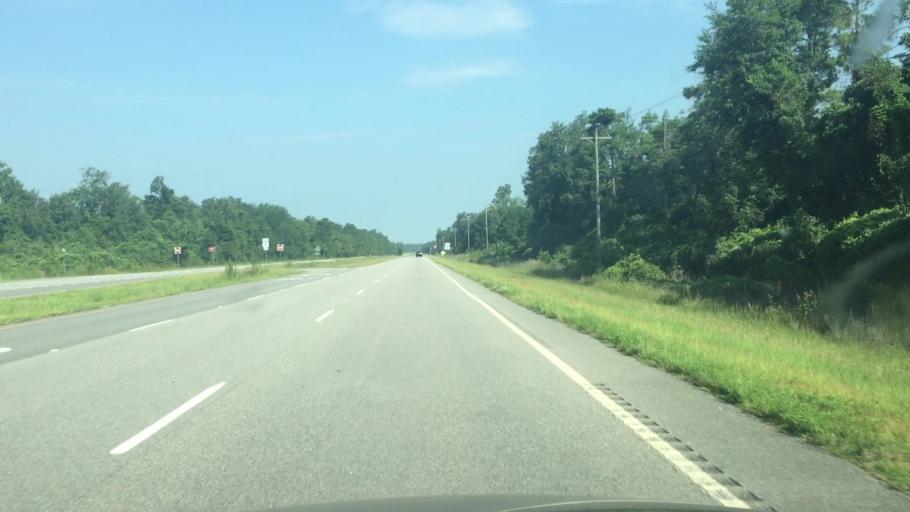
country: US
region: South Carolina
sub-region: Horry County
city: Loris
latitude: 34.0509
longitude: -78.8374
